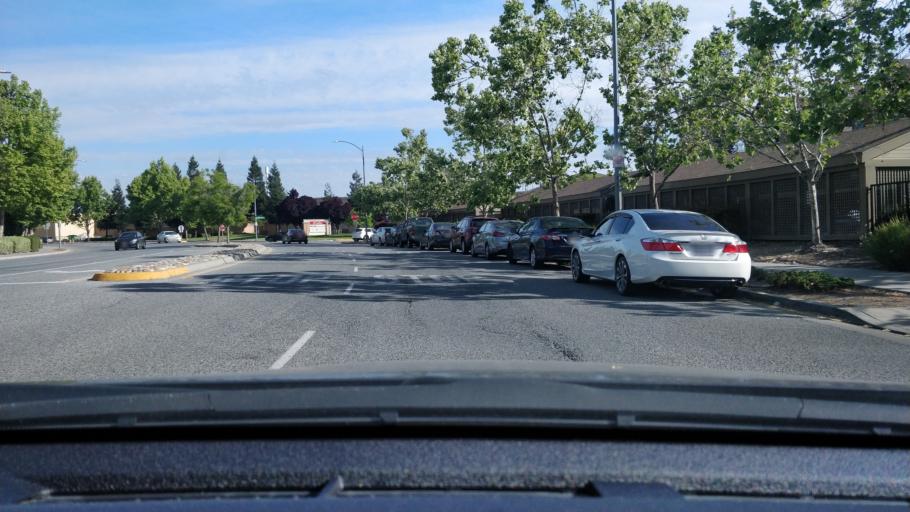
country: US
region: California
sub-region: Santa Clara County
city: Seven Trees
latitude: 37.2777
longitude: -121.8543
